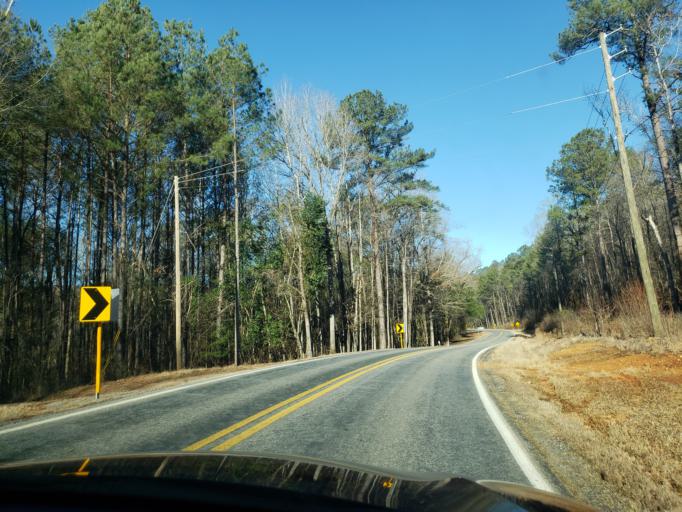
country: US
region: Alabama
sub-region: Elmore County
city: Eclectic
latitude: 32.6755
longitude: -85.9048
